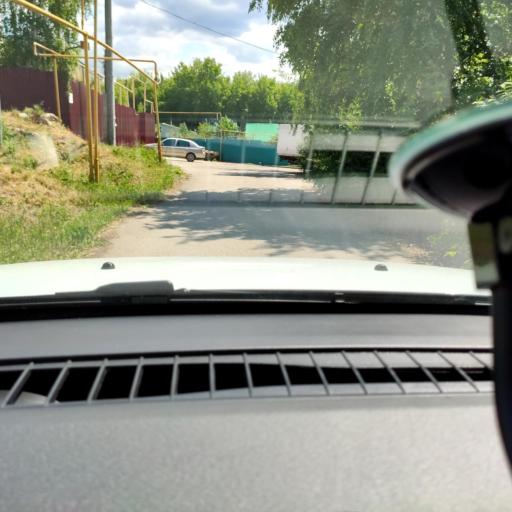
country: RU
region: Samara
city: Samara
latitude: 53.1761
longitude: 50.1632
